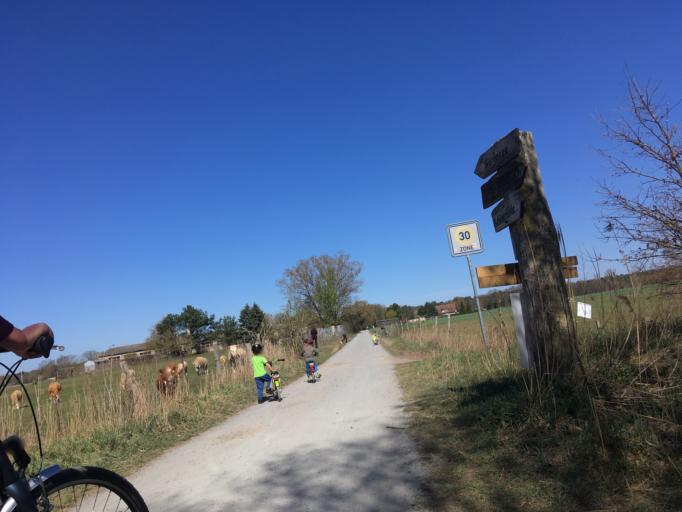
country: DE
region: Berlin
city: Buch
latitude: 52.6748
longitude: 13.4803
